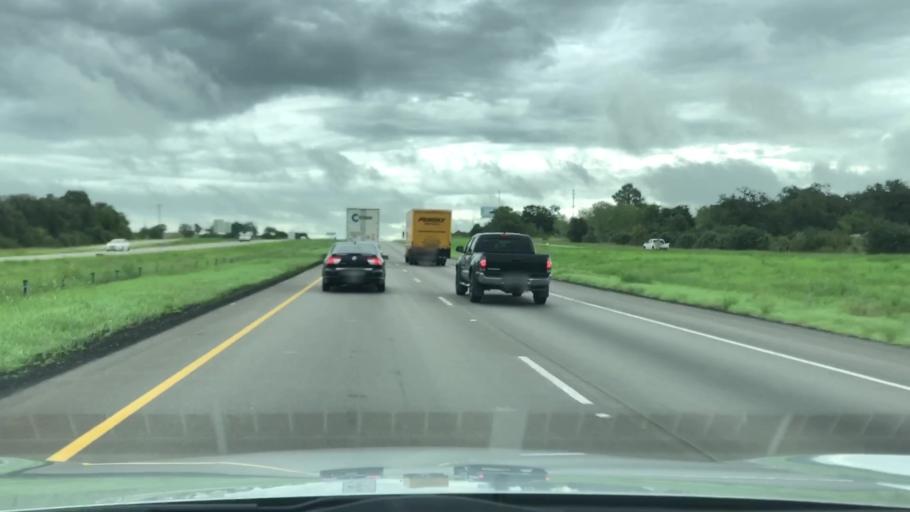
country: US
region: Texas
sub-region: Caldwell County
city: Luling
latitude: 29.6540
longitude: -97.5749
